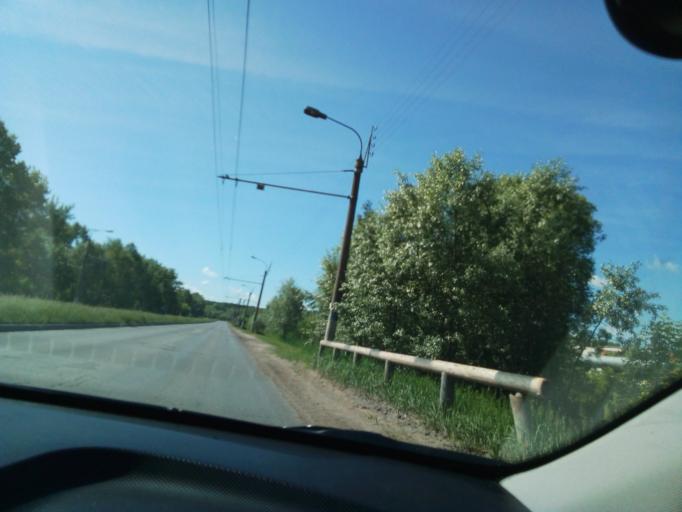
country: RU
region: Chuvashia
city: Novocheboksarsk
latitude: 56.0901
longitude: 47.5017
